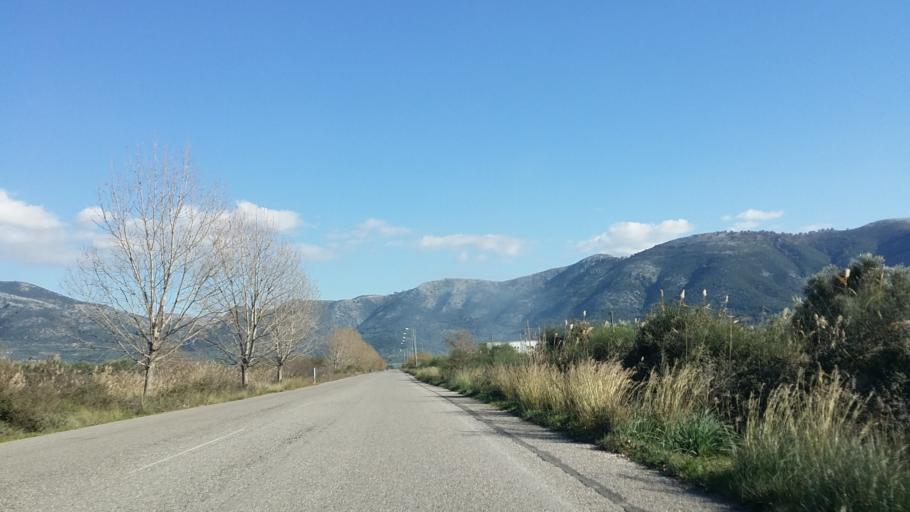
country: GR
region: West Greece
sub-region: Nomos Aitolias kai Akarnanias
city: Kandila
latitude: 38.6765
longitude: 20.9637
